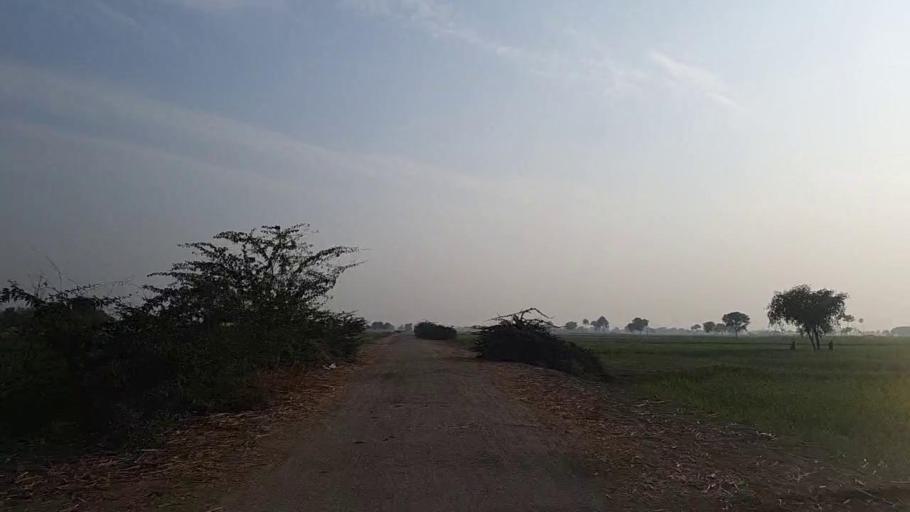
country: PK
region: Sindh
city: Jam Sahib
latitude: 26.3194
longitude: 68.5337
